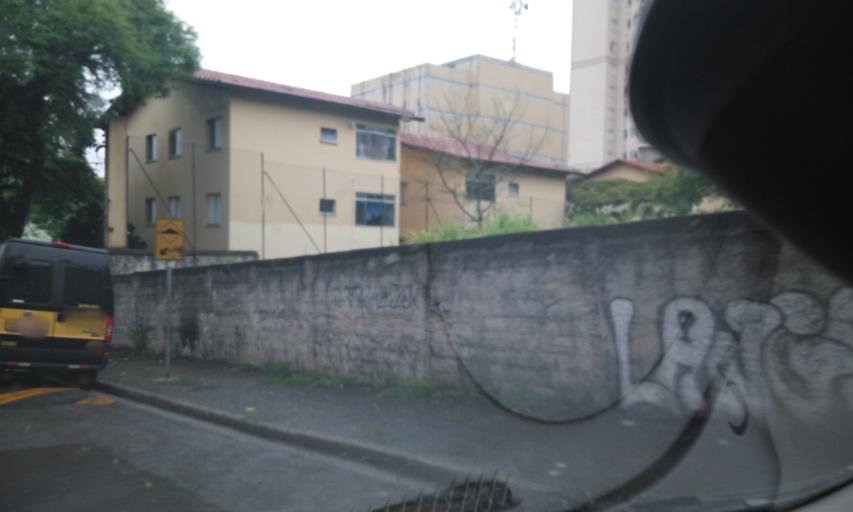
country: BR
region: Sao Paulo
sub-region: Sao Bernardo Do Campo
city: Sao Bernardo do Campo
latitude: -23.7226
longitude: -46.5726
